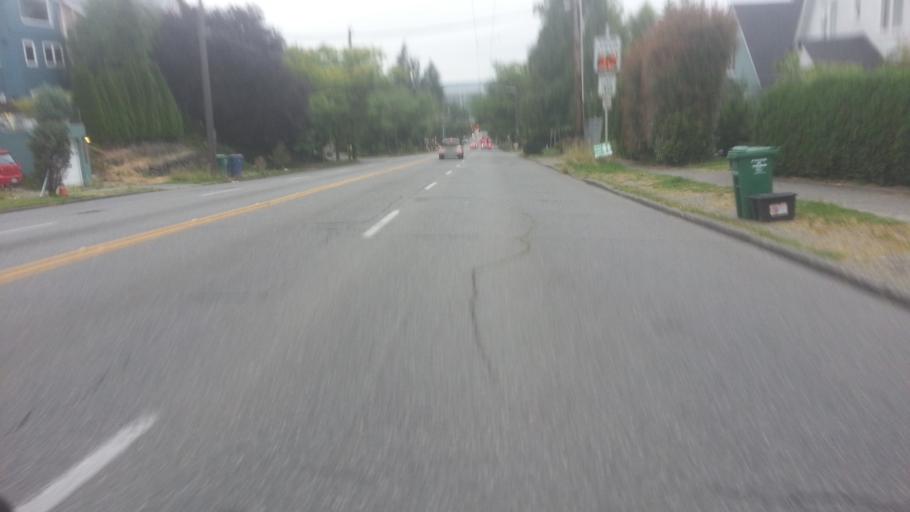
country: US
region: Washington
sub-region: King County
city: Seattle
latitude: 47.6306
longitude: -122.3016
